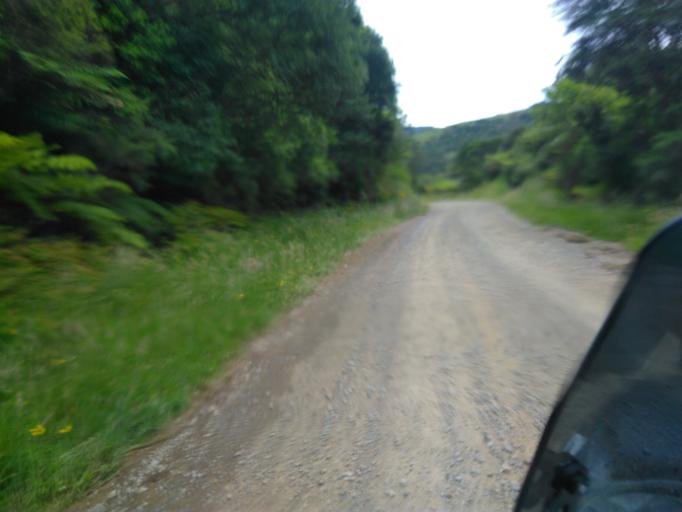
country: NZ
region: Bay of Plenty
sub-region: Opotiki District
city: Opotiki
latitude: -38.0313
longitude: 177.4410
